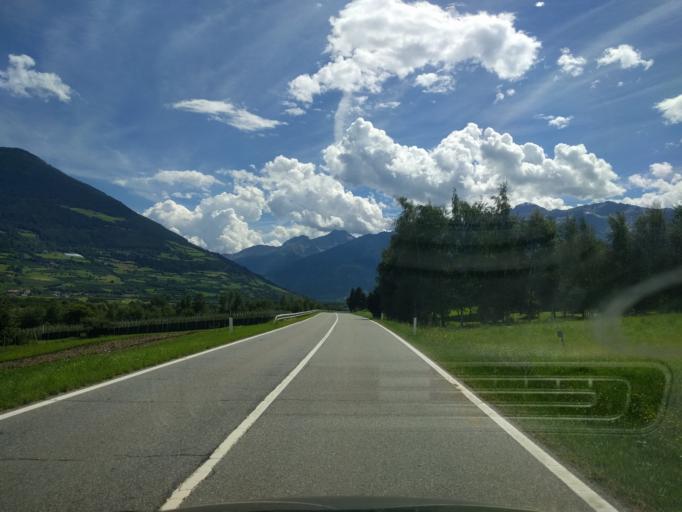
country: IT
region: Trentino-Alto Adige
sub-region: Bolzano
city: Glorenza
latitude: 46.6671
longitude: 10.5548
